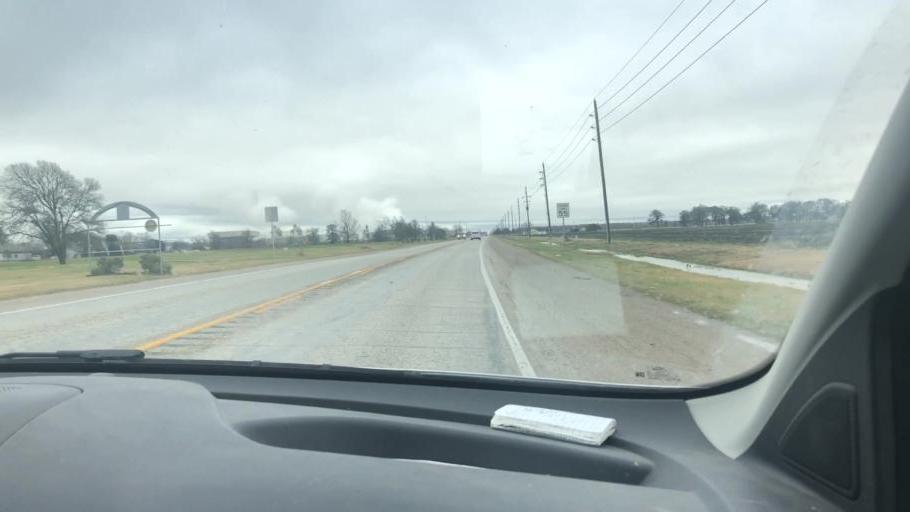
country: US
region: Texas
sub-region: Wharton County
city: Wharton
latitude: 29.3030
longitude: -96.0798
